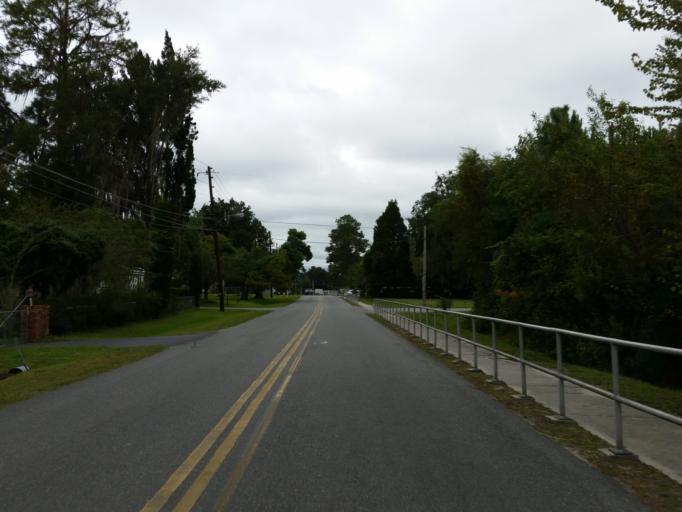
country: US
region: Florida
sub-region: Hamilton County
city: Jasper
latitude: 30.5203
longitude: -82.9598
